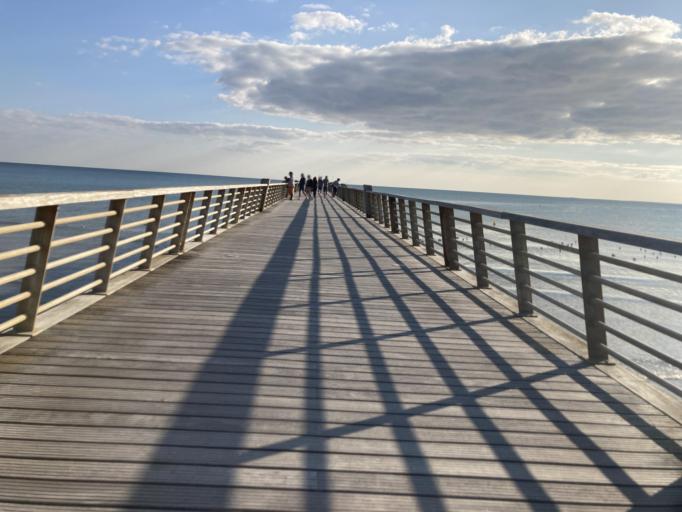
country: FR
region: Pays de la Loire
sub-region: Departement de la Vendee
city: Saint-Jean-de-Monts
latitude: 46.7863
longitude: -2.0837
